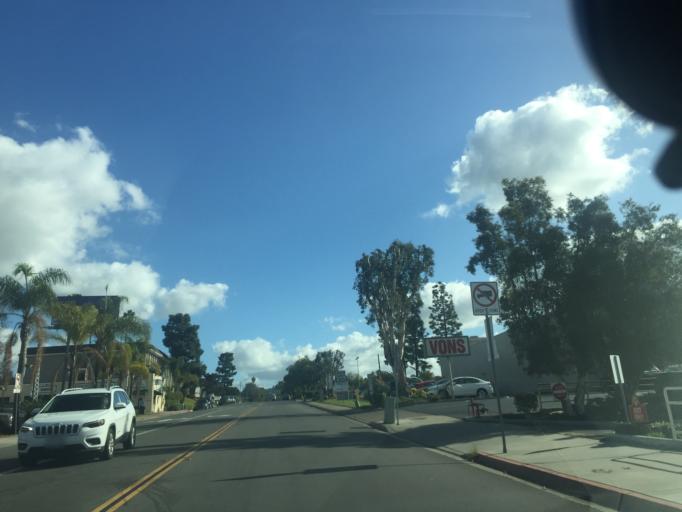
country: US
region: California
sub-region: San Diego County
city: La Mesa
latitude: 32.7930
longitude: -117.0972
